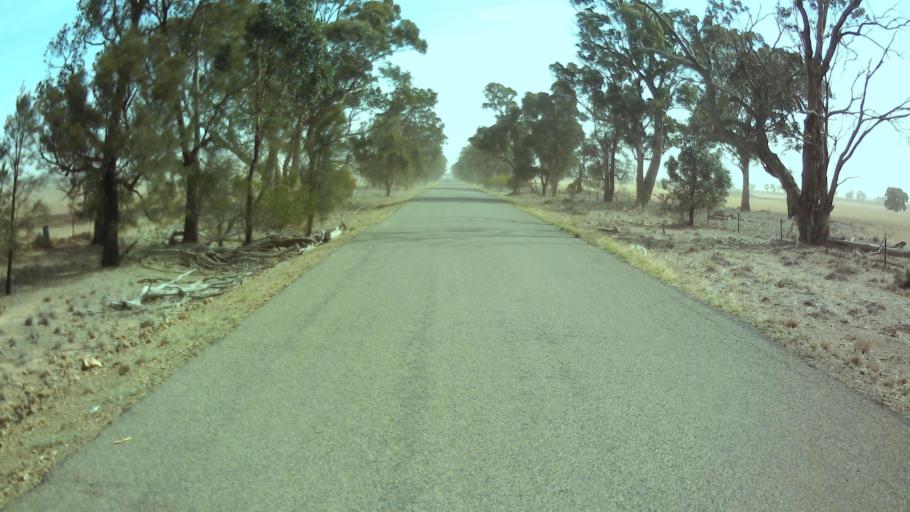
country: AU
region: New South Wales
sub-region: Weddin
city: Grenfell
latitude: -33.7603
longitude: 147.9889
